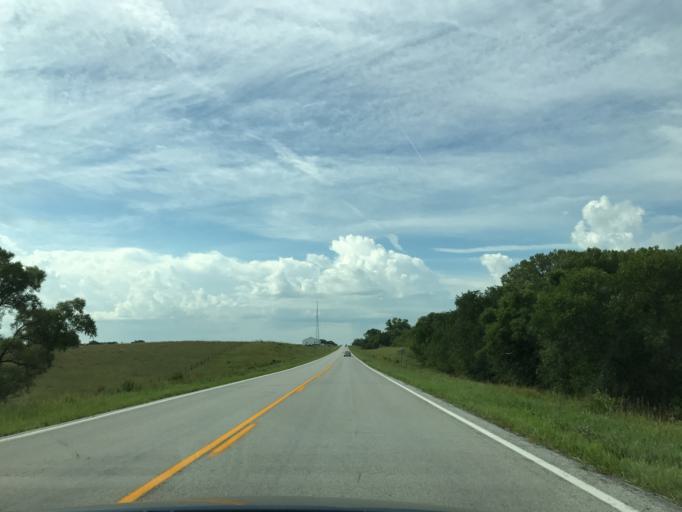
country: US
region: Nebraska
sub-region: Saline County
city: Friend
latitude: 40.5319
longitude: -97.1792
